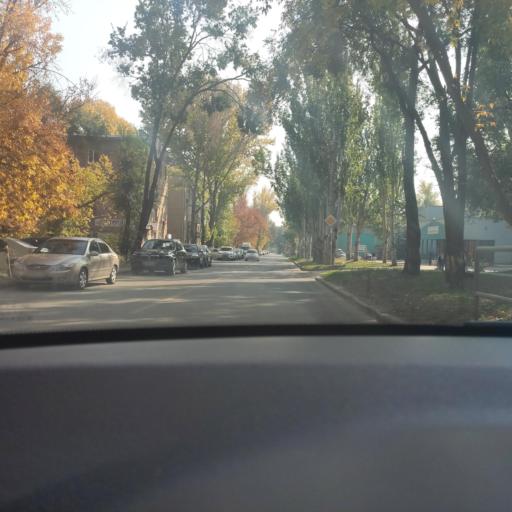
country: RU
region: Samara
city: Samara
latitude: 53.2072
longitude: 50.2282
